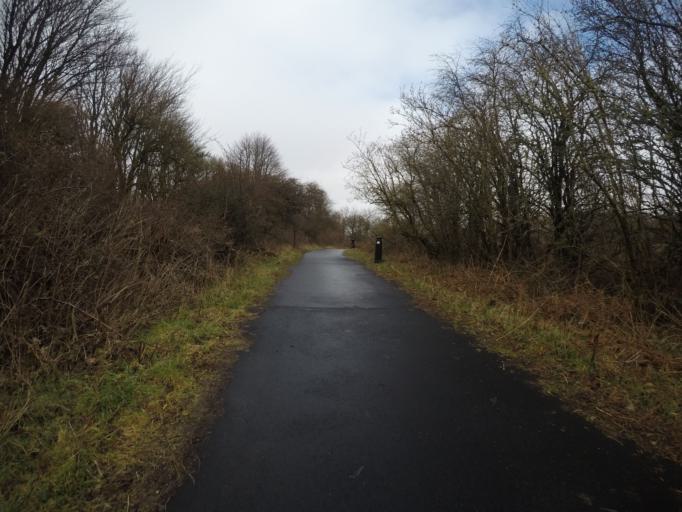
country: GB
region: Scotland
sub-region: North Ayrshire
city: Fairlie
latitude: 55.7329
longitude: -4.8637
